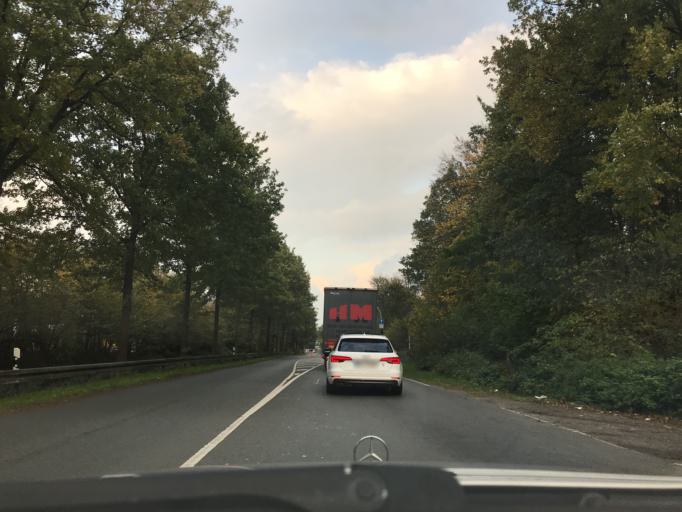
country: DE
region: North Rhine-Westphalia
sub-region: Regierungsbezirk Munster
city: Gelsenkirchen
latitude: 51.4963
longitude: 7.0996
